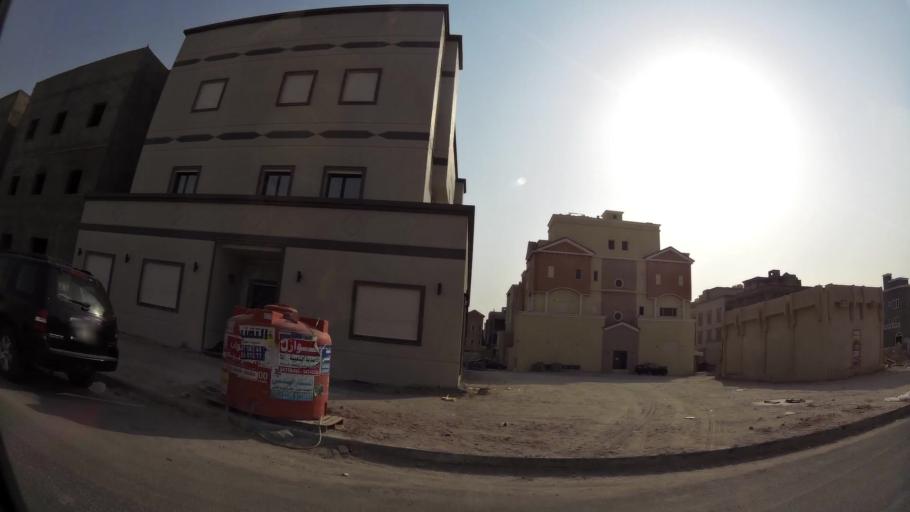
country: KW
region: Al Asimah
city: Ar Rabiyah
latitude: 29.3261
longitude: 47.8107
